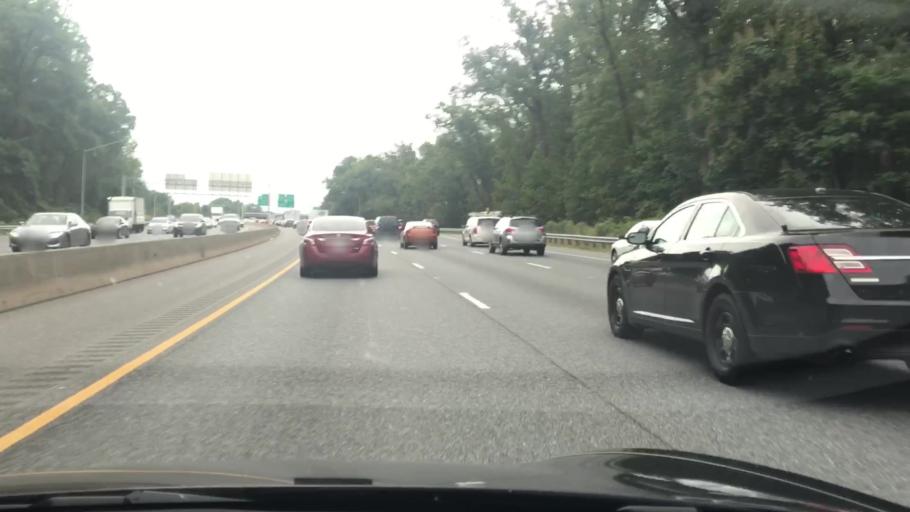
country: US
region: Maryland
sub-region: Baltimore County
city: Hampton
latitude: 39.4146
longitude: -76.5937
